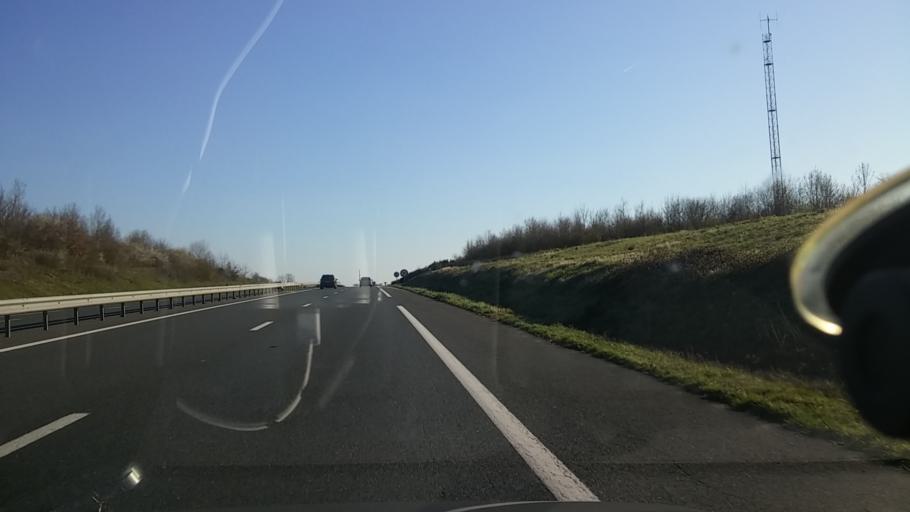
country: FR
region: Centre
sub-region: Departement de l'Indre
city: Argenton-sur-Creuse
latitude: 46.5480
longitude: 1.5061
